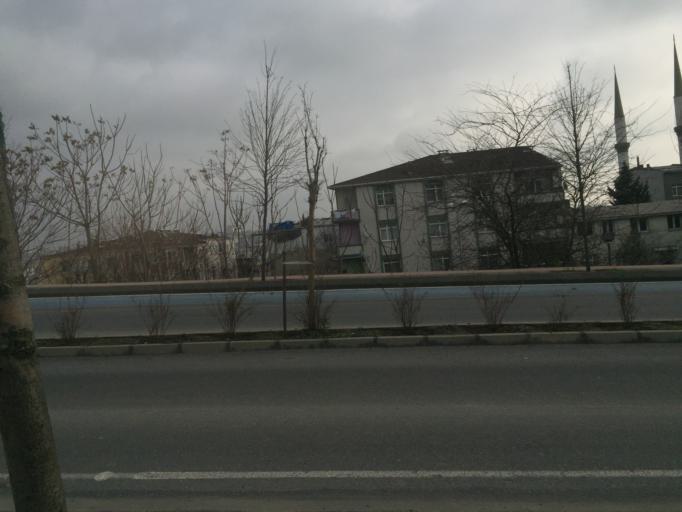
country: TR
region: Istanbul
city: merter keresteciler
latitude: 41.0274
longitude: 28.8938
